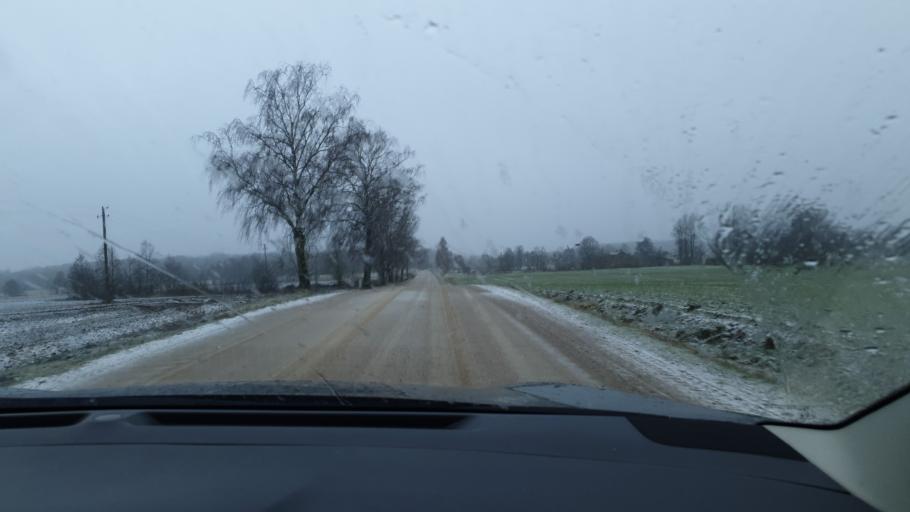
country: LT
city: Jieznas
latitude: 54.5757
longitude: 24.3172
